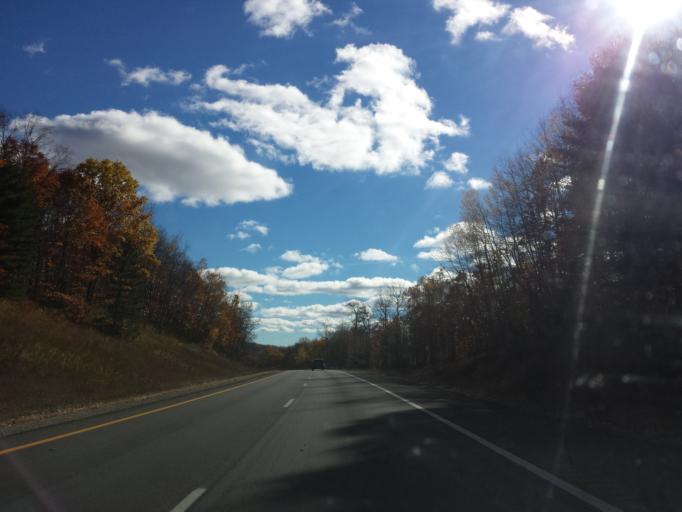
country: US
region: Michigan
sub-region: Cheboygan County
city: Indian River
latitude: 45.3538
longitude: -84.6147
